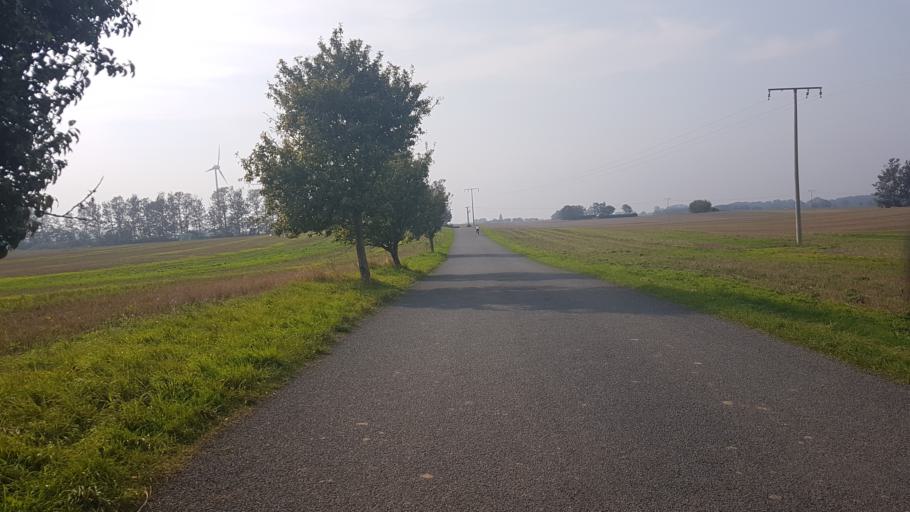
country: DE
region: Mecklenburg-Vorpommern
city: Garz
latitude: 54.2949
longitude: 13.3690
